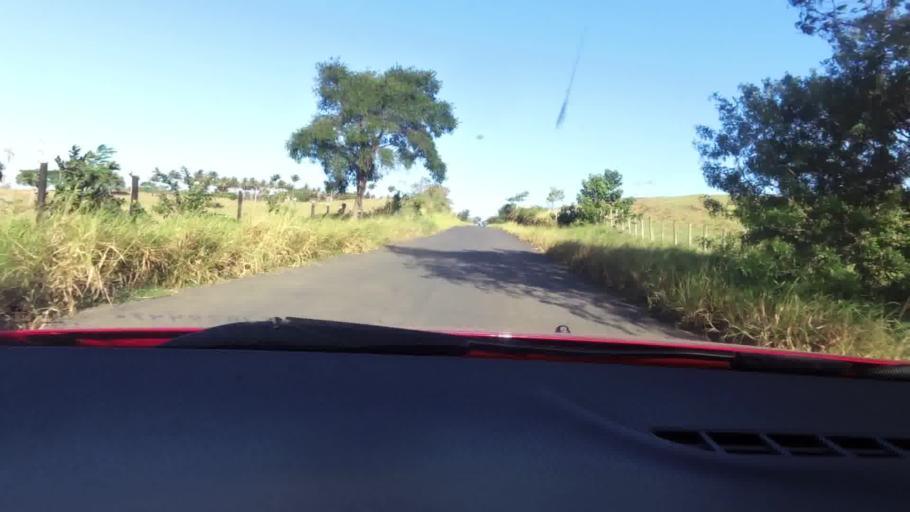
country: BR
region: Espirito Santo
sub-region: Guarapari
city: Guarapari
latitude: -20.5265
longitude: -40.4744
